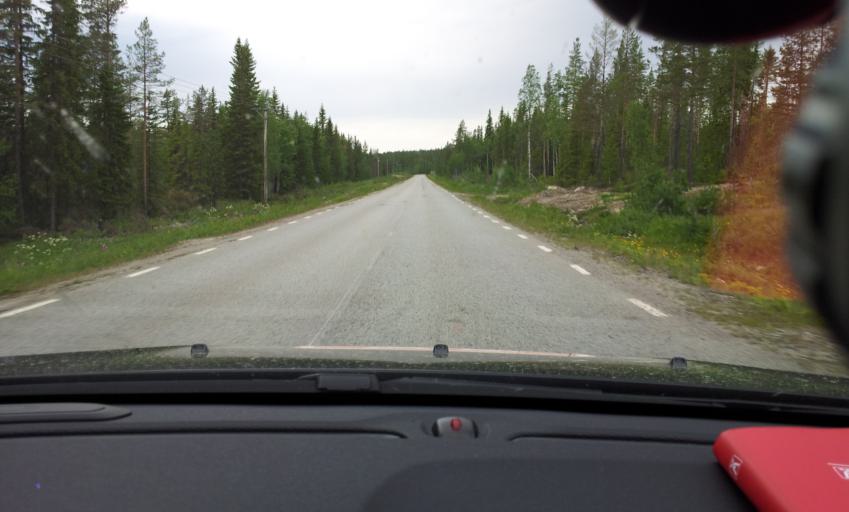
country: SE
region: Jaemtland
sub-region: Bergs Kommun
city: Hoverberg
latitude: 62.6770
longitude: 14.6719
